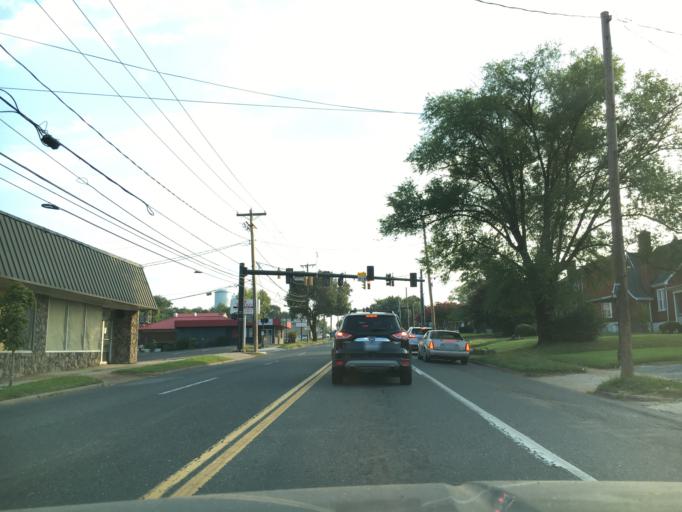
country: US
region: Virginia
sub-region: City of Lynchburg
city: West Lynchburg
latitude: 37.3792
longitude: -79.1833
